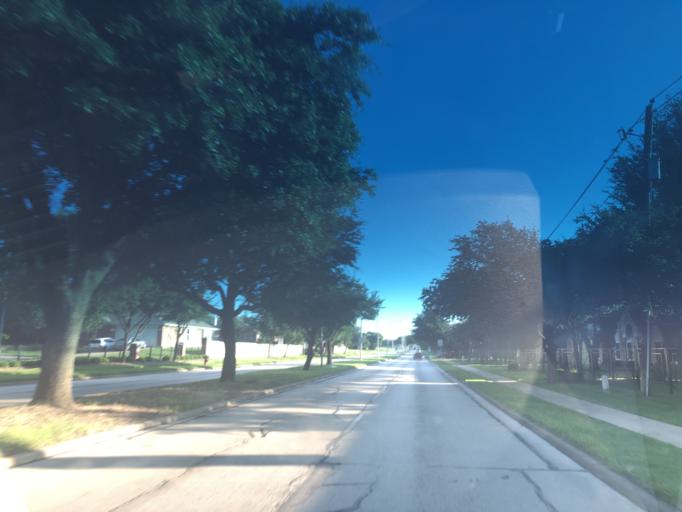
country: US
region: Texas
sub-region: Dallas County
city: Grand Prairie
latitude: 32.7001
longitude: -97.0155
